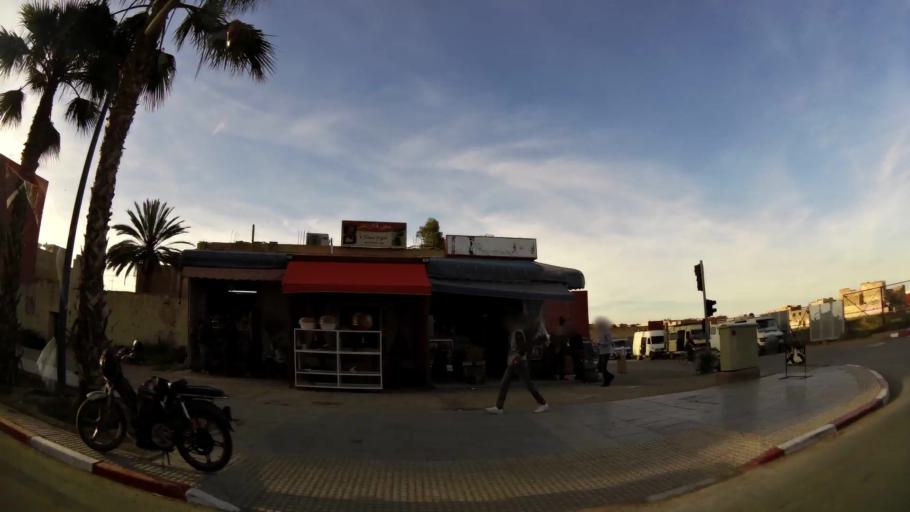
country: MA
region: Oriental
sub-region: Oujda-Angad
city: Oujda
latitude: 34.6792
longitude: -1.9000
